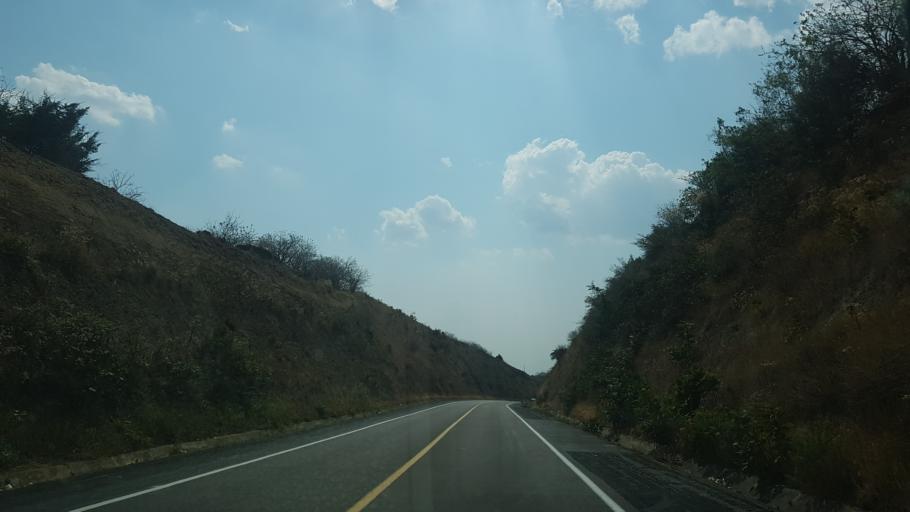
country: MX
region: Puebla
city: San Juan Amecac
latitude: 18.8156
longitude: -98.6719
